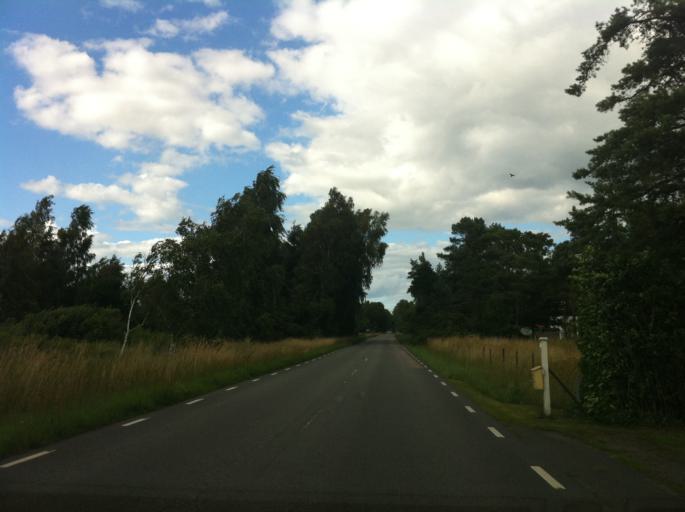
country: SE
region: Skane
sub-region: Simrishamns Kommun
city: Simrishamn
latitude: 55.4095
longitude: 14.1922
